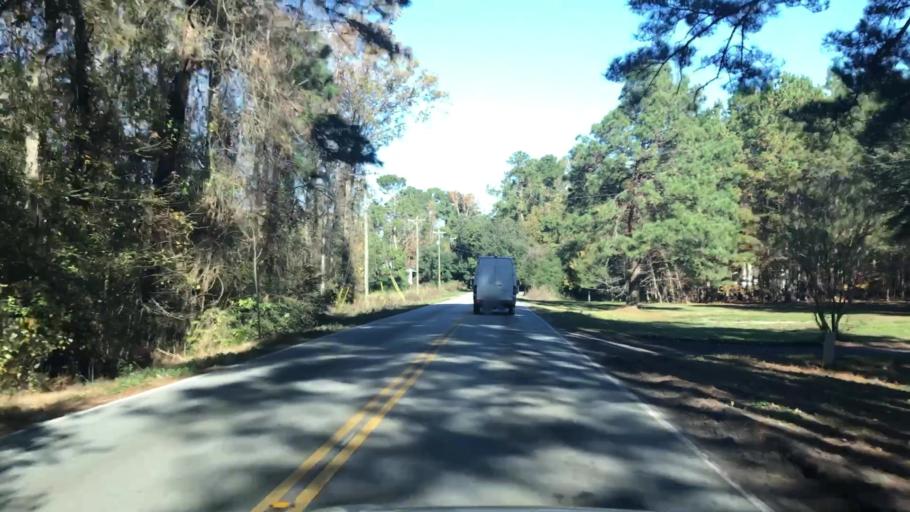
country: US
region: South Carolina
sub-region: Dorchester County
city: Summerville
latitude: 33.0180
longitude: -80.2400
